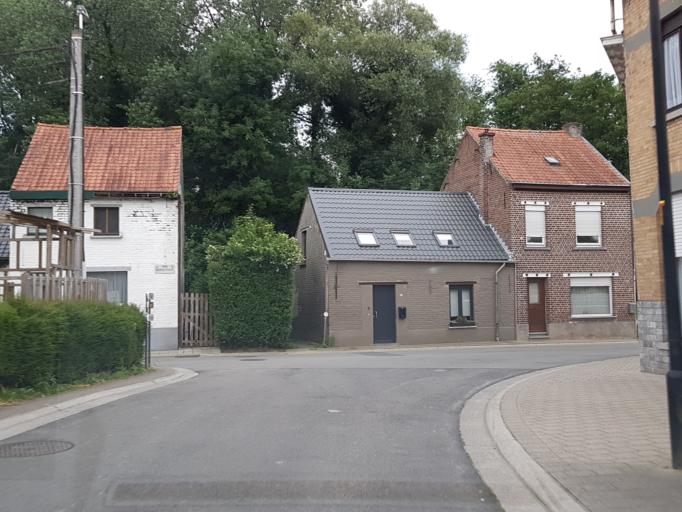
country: BE
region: Flanders
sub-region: Provincie Vlaams-Brabant
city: Asse
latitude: 50.9039
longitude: 4.1662
